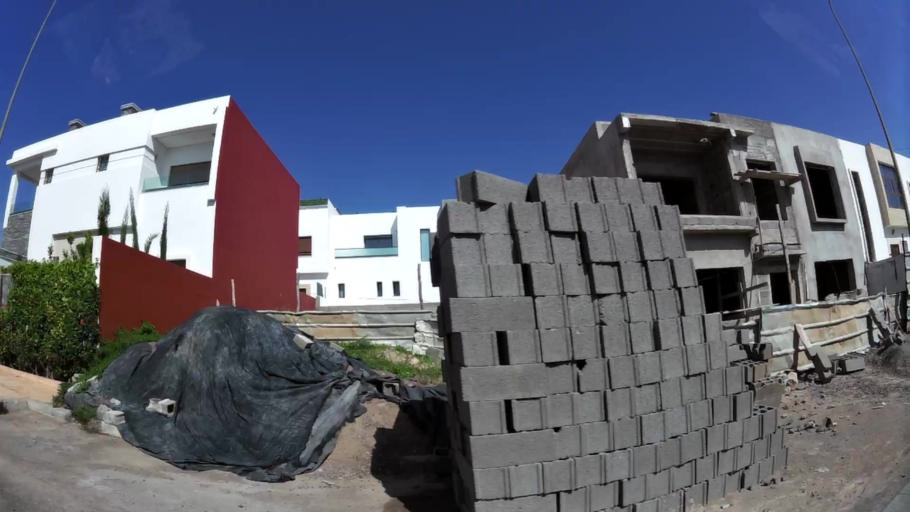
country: MA
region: Souss-Massa-Draa
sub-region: Agadir-Ida-ou-Tnan
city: Agadir
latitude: 30.3948
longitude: -9.5920
